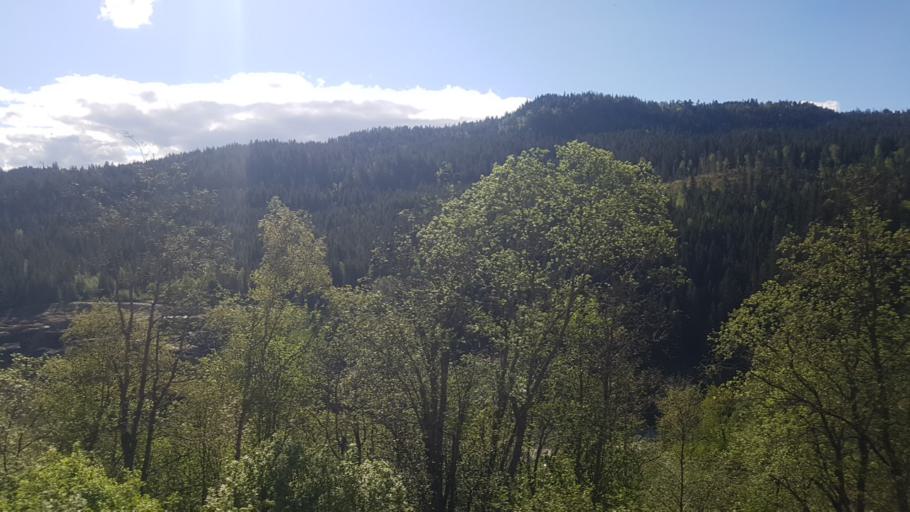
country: NO
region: Sor-Trondelag
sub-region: Midtre Gauldal
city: Storen
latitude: 62.9434
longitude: 10.1876
